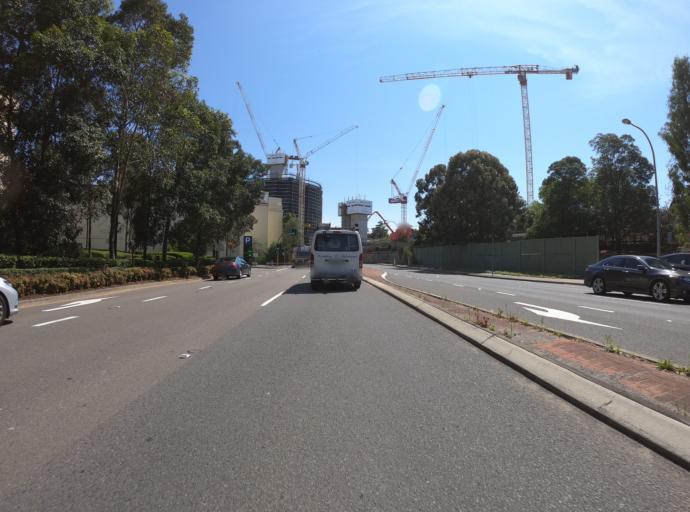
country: AU
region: New South Wales
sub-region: The Hills Shire
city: Castle Hill
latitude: -33.7297
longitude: 151.0084
